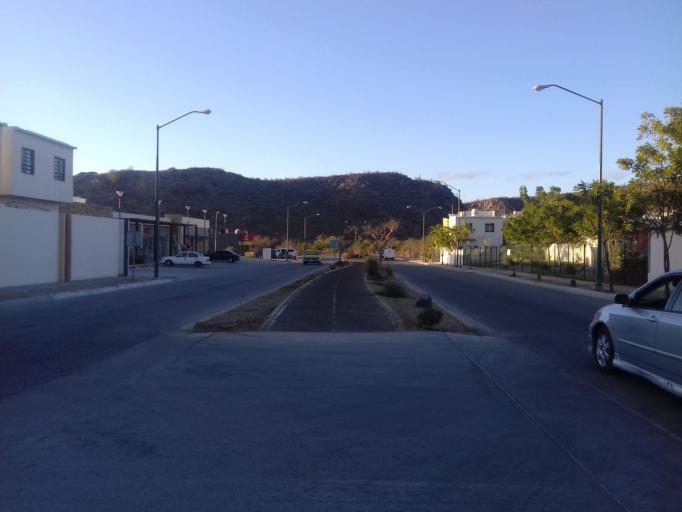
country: MX
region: Baja California Sur
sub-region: La Paz
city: La Paz
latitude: 24.0898
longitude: -110.2981
